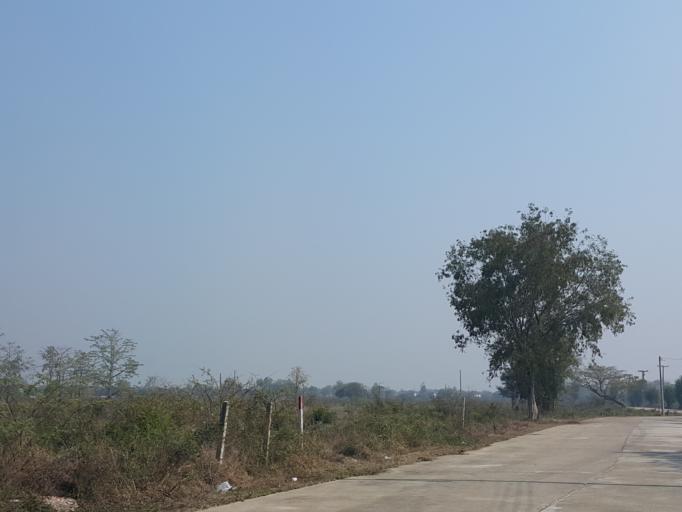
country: TH
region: Chiang Mai
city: San Kamphaeng
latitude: 18.7841
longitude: 99.0765
